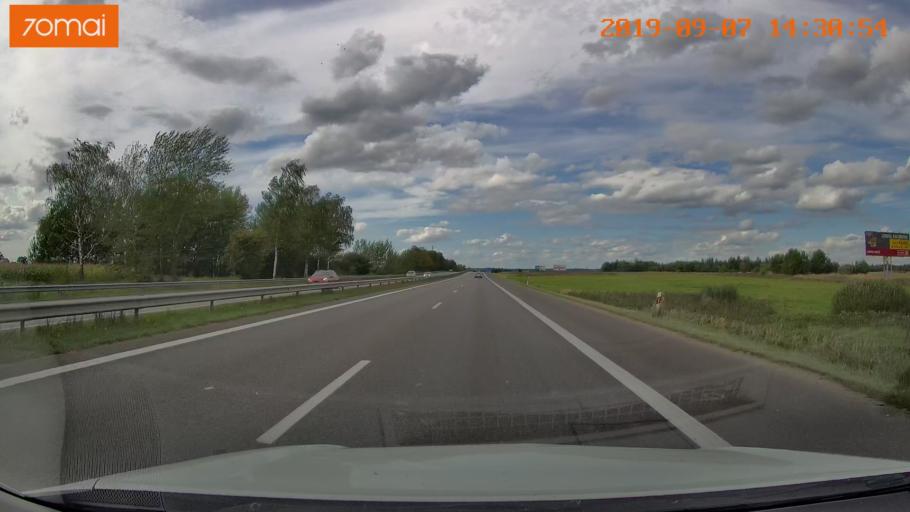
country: LT
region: Kauno apskritis
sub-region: Kauno rajonas
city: Karmelava
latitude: 54.8712
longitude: 24.2357
